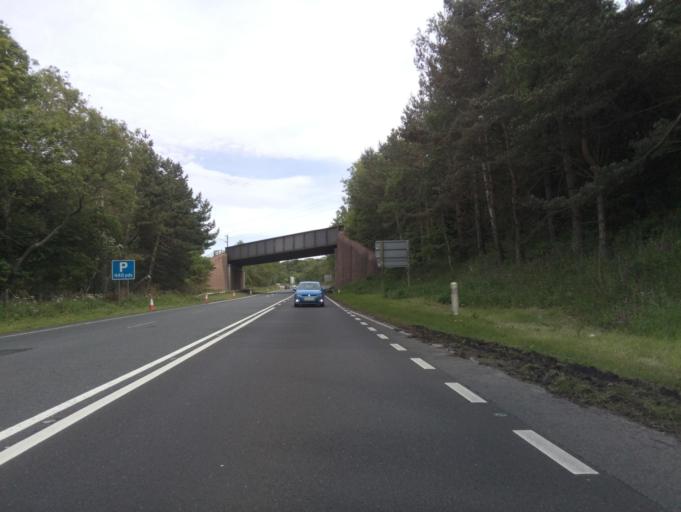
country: GB
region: Scotland
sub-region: The Scottish Borders
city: Eyemouth
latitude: 55.8441
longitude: -2.0928
